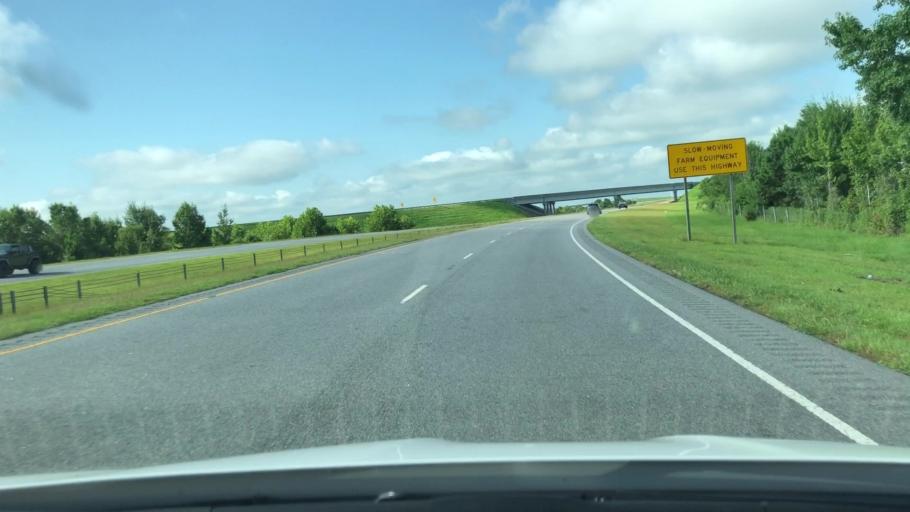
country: US
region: North Carolina
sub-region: Pasquotank County
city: Elizabeth City
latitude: 36.3738
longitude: -76.3097
